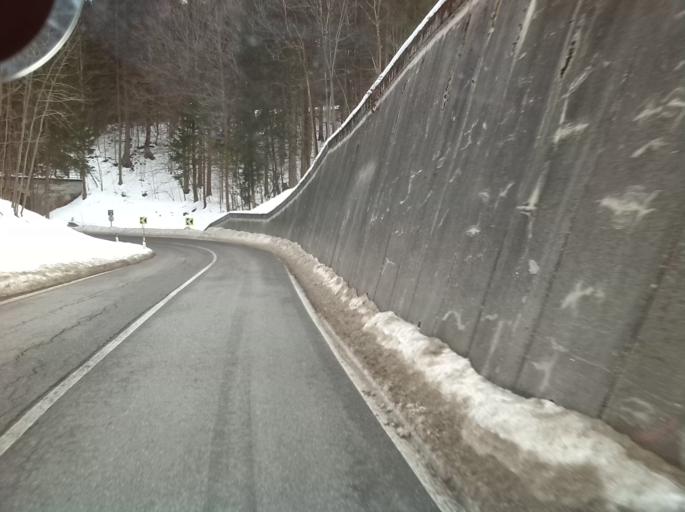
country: IT
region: Friuli Venezia Giulia
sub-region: Provincia di Udine
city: Tarvisio
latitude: 46.5053
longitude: 13.6197
